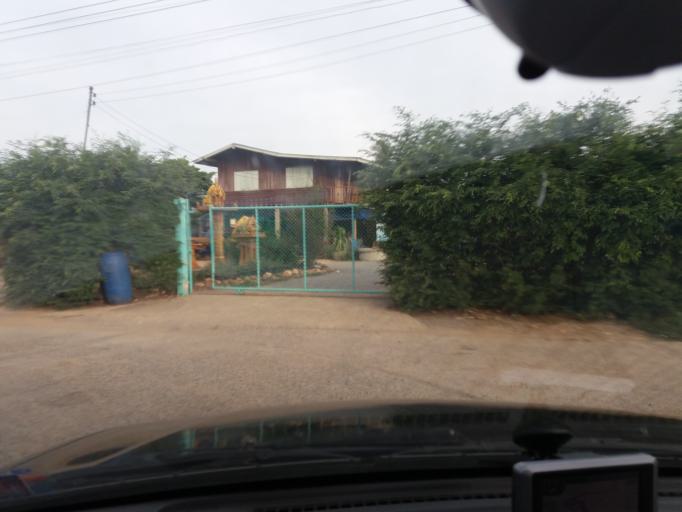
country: TH
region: Suphan Buri
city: Doembang Nangbuat
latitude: 14.8303
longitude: 100.1345
